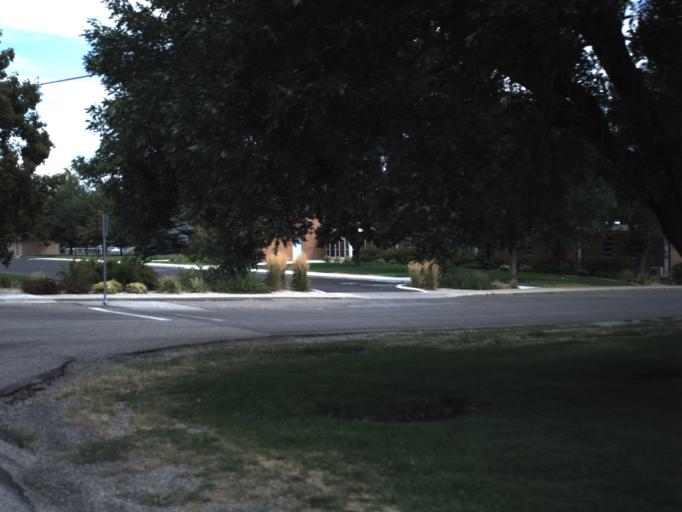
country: US
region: Utah
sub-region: Cache County
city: Mendon
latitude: 41.7077
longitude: -111.9793
